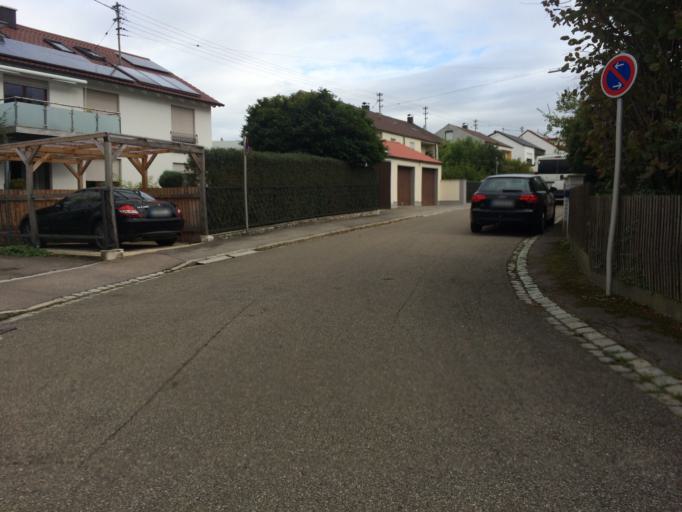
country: DE
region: Bavaria
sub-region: Swabia
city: Friedberg
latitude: 48.3508
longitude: 10.9882
